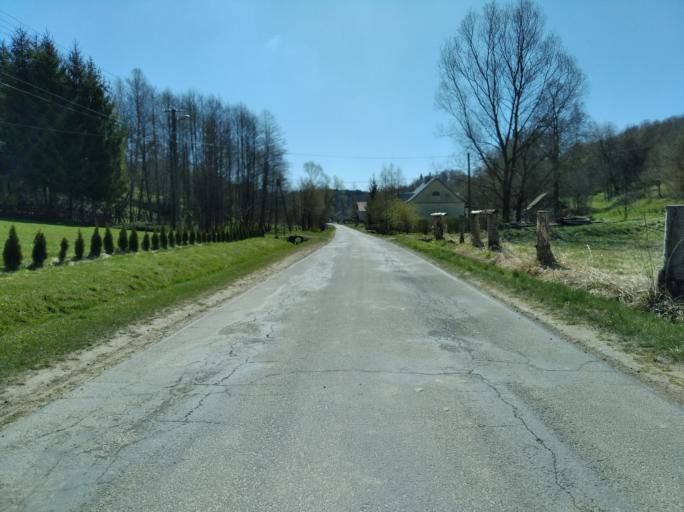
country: PL
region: Subcarpathian Voivodeship
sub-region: Powiat brzozowski
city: Jablonka
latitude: 49.7333
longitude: 22.1460
